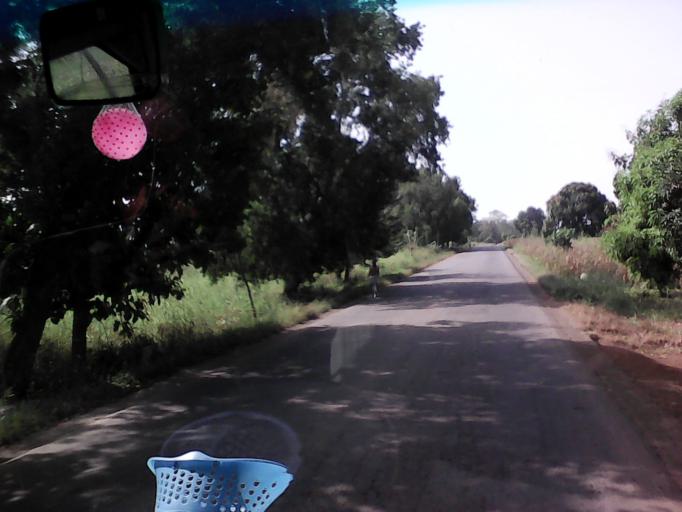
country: TG
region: Centrale
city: Sokode
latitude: 8.8943
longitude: 1.0880
